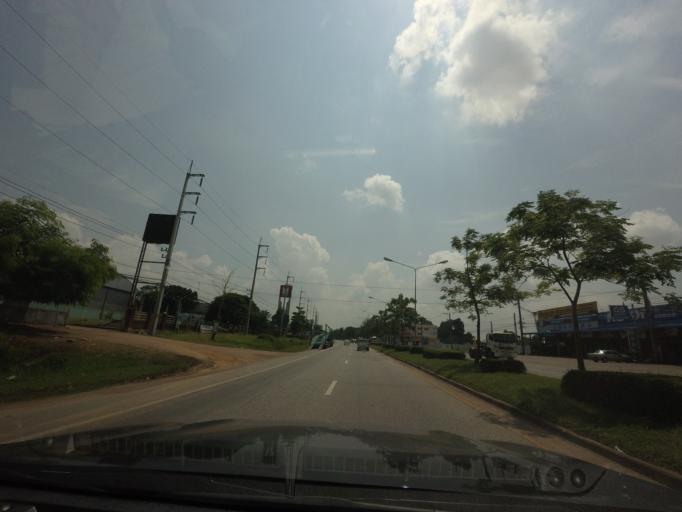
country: TH
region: Uttaradit
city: Uttaradit
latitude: 17.6029
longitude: 100.1241
